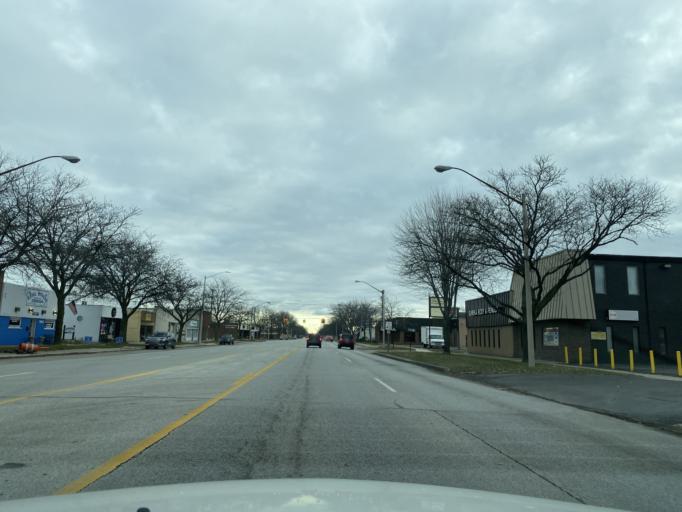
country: US
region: Michigan
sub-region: Wayne County
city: Southgate
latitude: 42.1995
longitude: -83.1745
